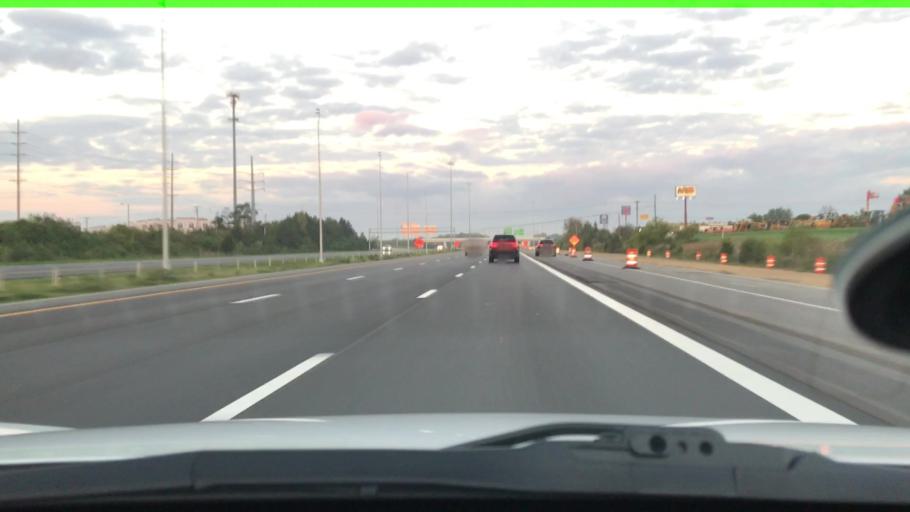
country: US
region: Ohio
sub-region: Franklin County
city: Lincoln Village
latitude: 39.9772
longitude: -83.1420
